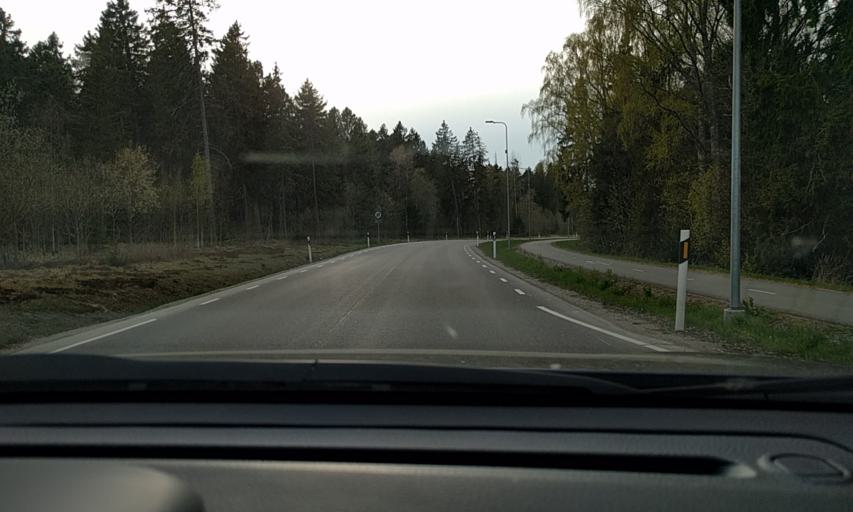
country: EE
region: Harju
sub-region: Viimsi vald
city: Viimsi
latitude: 59.5221
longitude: 24.8935
